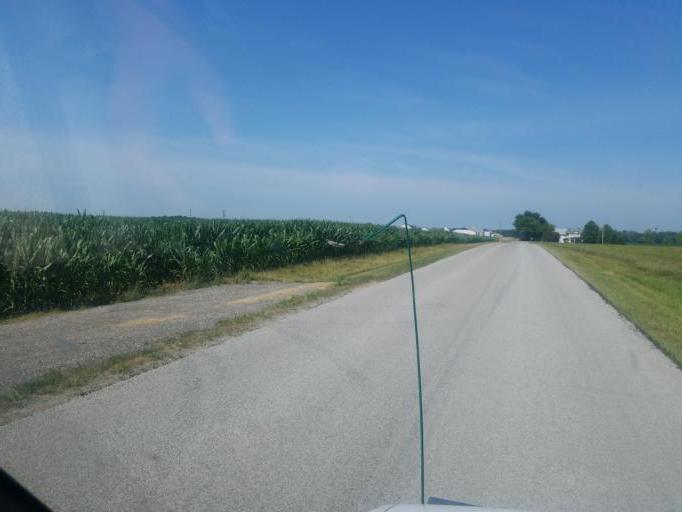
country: US
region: Ohio
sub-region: Union County
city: Marysville
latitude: 40.2742
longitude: -83.3723
